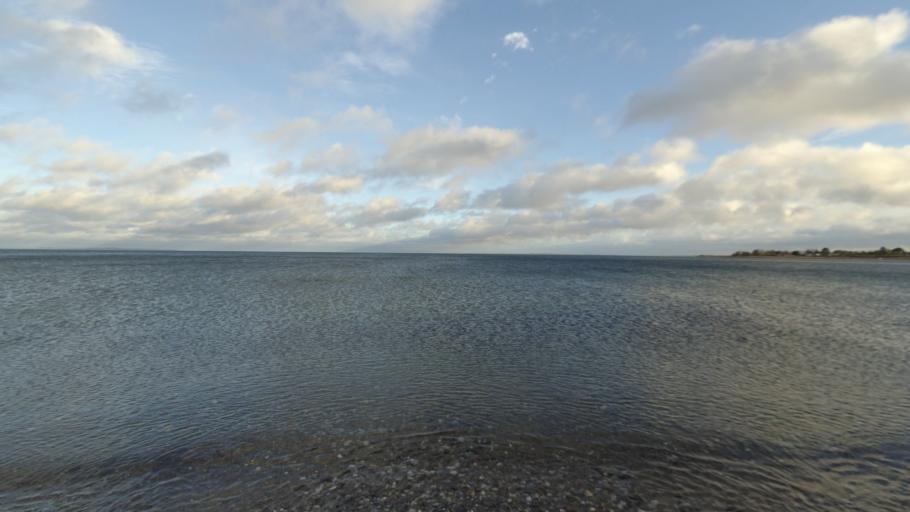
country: DK
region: Central Jutland
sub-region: Arhus Kommune
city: Beder
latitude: 56.0278
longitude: 10.2663
